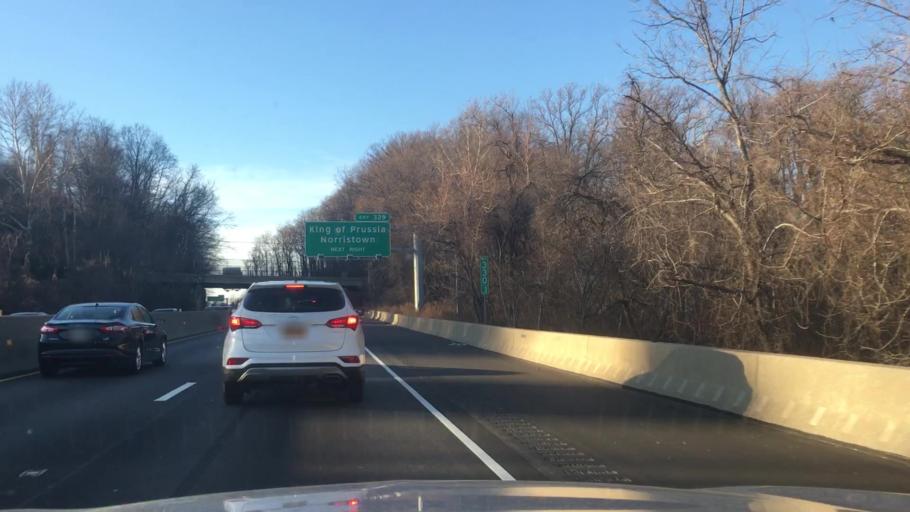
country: US
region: Pennsylvania
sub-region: Montgomery County
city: West Conshohocken
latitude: 40.0710
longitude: -75.3445
